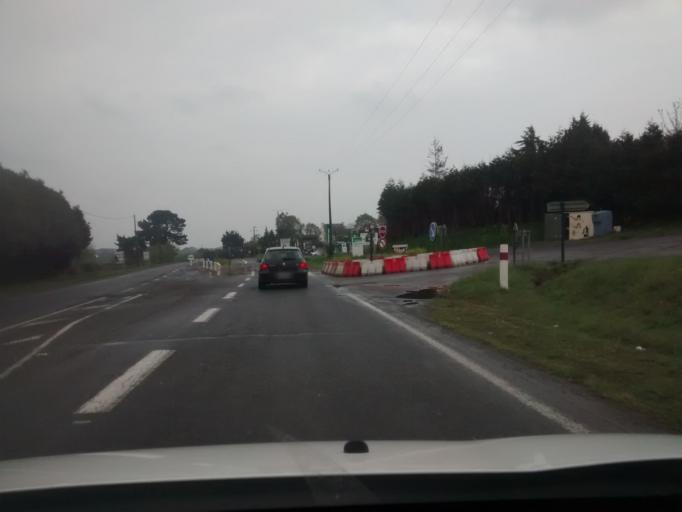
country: FR
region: Brittany
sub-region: Departement des Cotes-d'Armor
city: Saint-Quay-Perros
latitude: 48.7696
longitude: -3.4467
